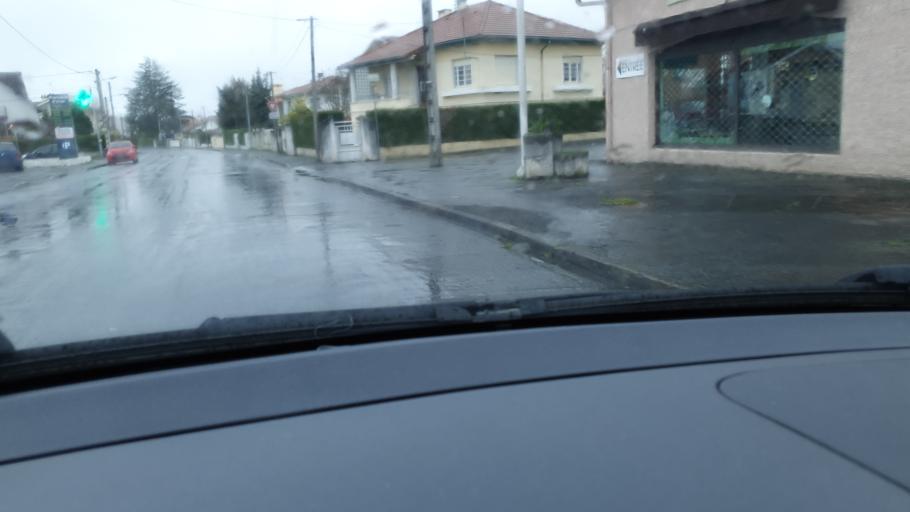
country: FR
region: Midi-Pyrenees
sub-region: Departement des Hautes-Pyrenees
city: Tarbes
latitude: 43.2429
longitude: 0.0538
